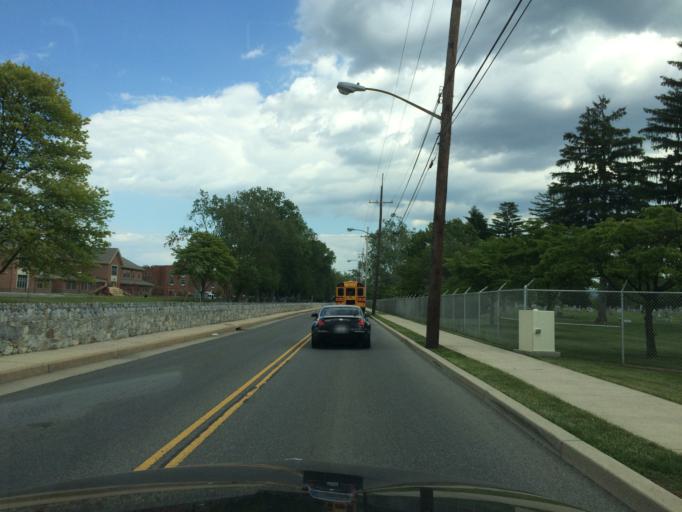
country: US
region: Maryland
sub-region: Washington County
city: Hagerstown
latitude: 39.6320
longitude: -77.7222
